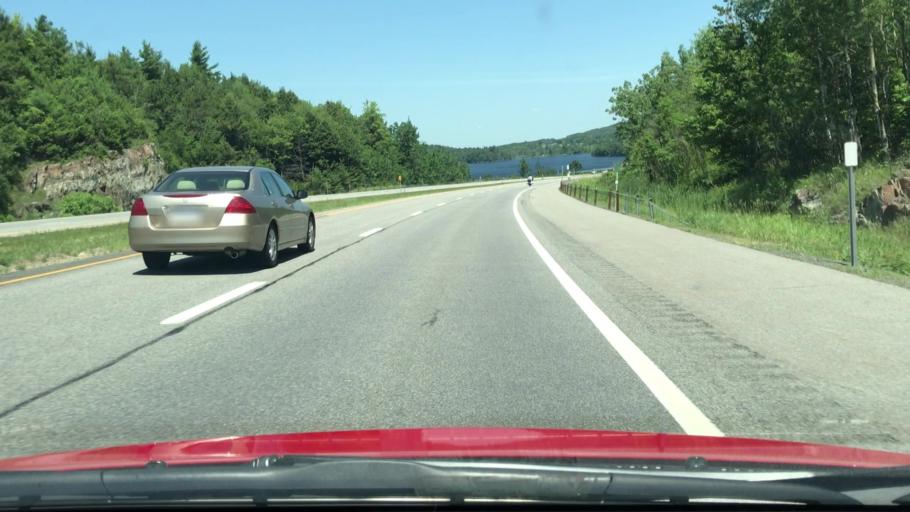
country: US
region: New York
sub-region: Essex County
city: Keeseville
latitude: 44.4160
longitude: -73.4973
